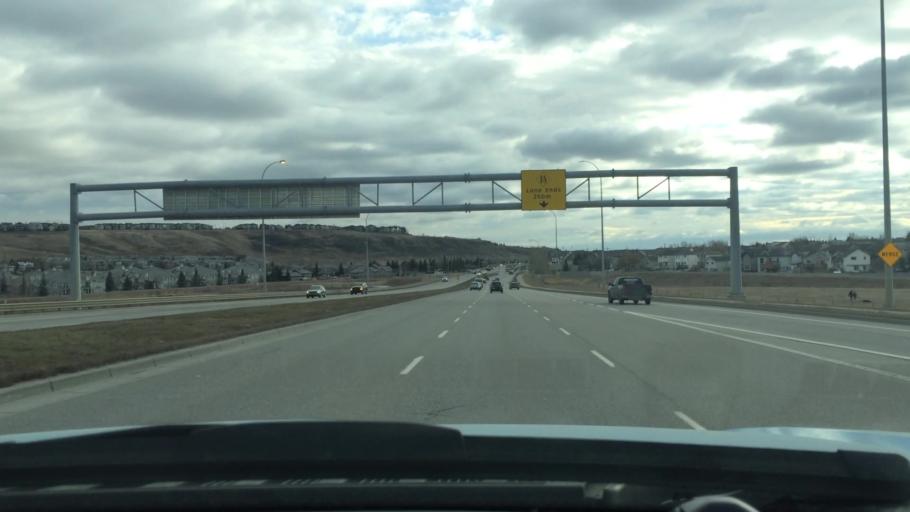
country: CA
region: Alberta
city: Calgary
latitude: 51.1557
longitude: -114.1137
